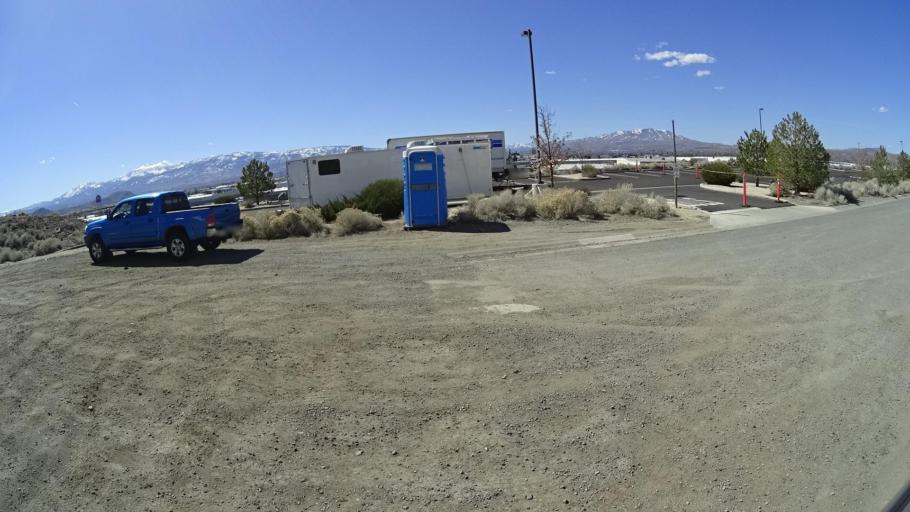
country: US
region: Nevada
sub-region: Washoe County
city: Sparks
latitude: 39.5312
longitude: -119.7002
